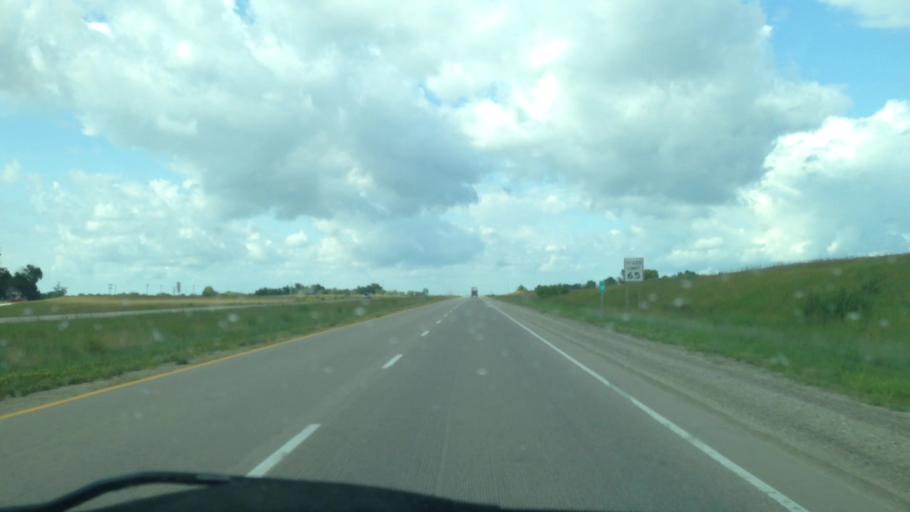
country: US
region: Illinois
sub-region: Hancock County
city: Nauvoo
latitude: 40.5919
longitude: -91.5631
